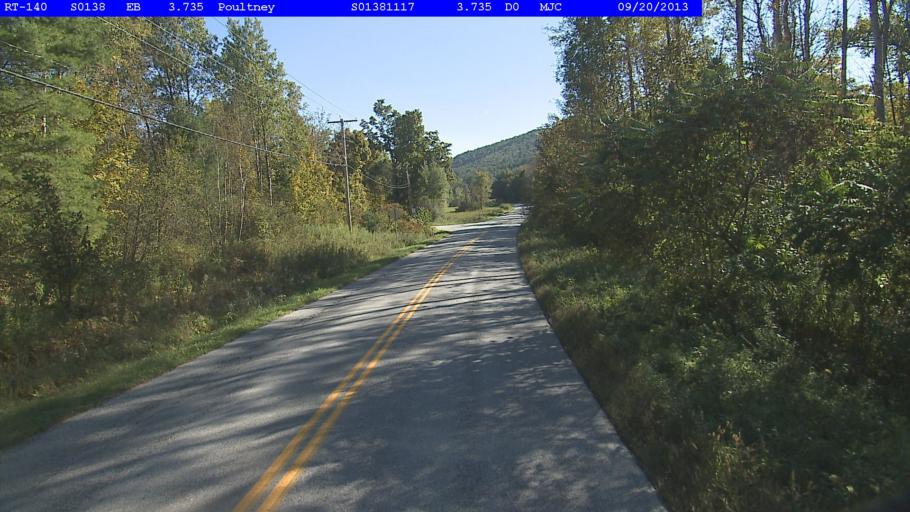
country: US
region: Vermont
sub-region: Rutland County
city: Poultney
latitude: 43.5120
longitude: -73.1770
